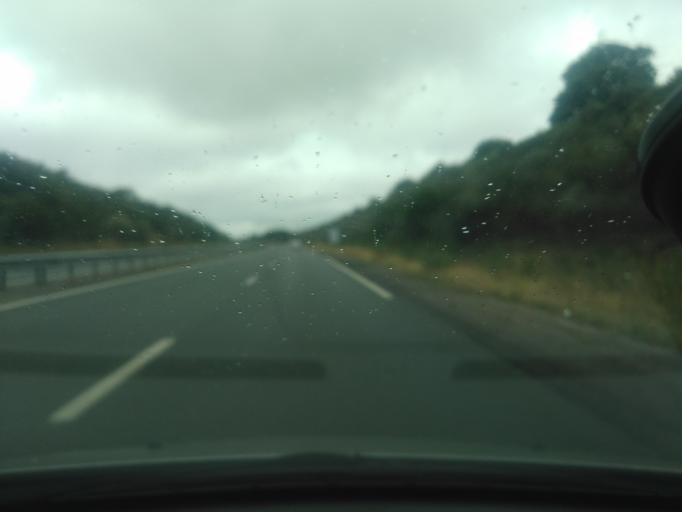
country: FR
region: Brittany
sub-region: Departement des Cotes-d'Armor
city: Pledeliac
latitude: 48.4135
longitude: -2.3815
